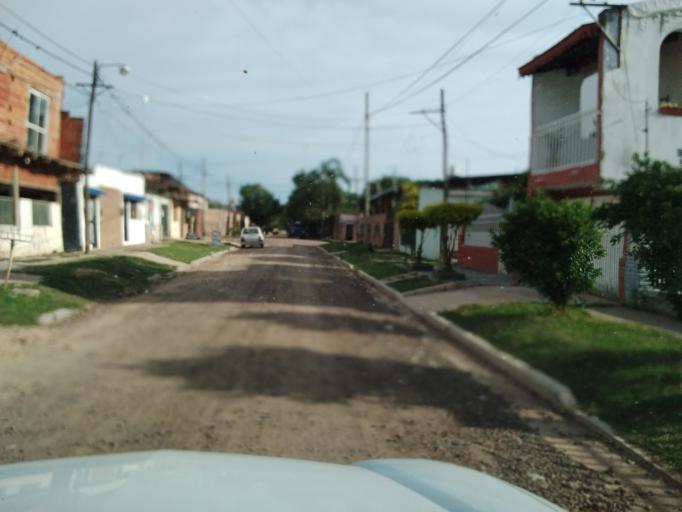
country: AR
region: Corrientes
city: Corrientes
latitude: -27.4915
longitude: -58.8423
